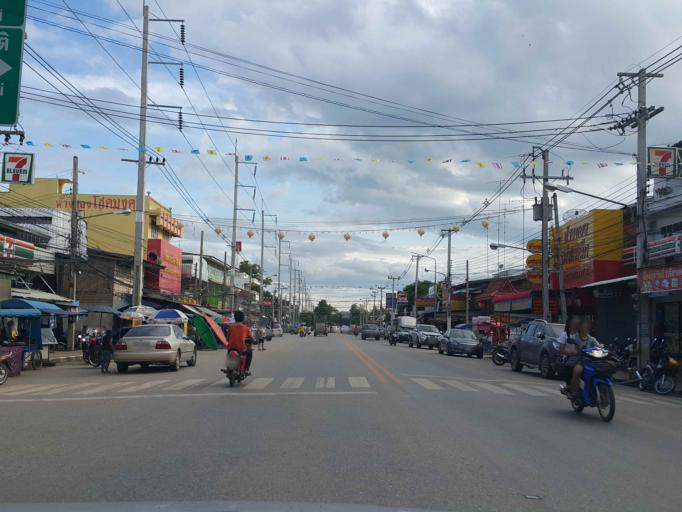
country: TH
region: Sukhothai
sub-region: Amphoe Si Satchanalai
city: Si Satchanalai
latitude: 17.5171
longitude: 99.7628
